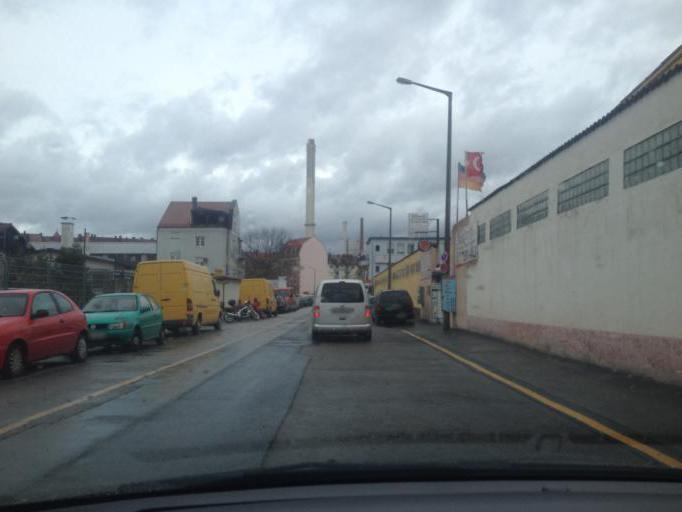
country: DE
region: Bavaria
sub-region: Regierungsbezirk Mittelfranken
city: Nuernberg
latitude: 49.4333
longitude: 11.0615
